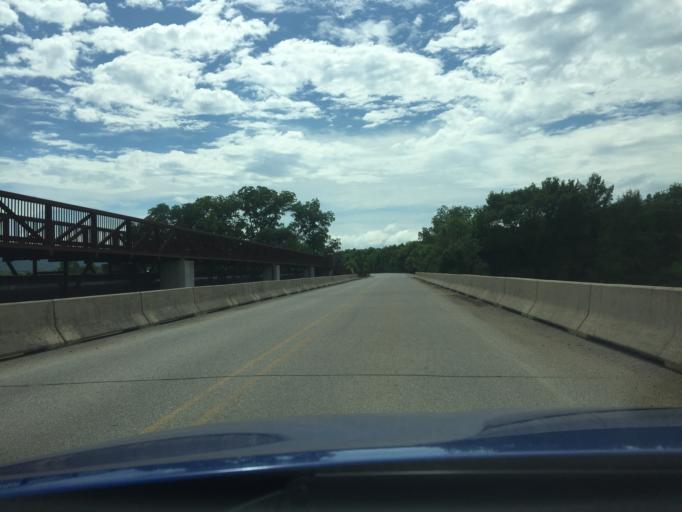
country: US
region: Arkansas
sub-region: Pulaski County
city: Maumelle
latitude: 34.8170
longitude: -92.4393
